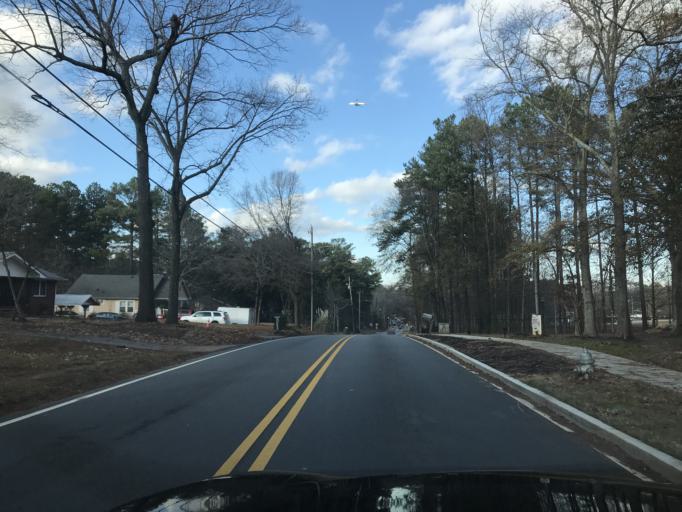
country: US
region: Georgia
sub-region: Fulton County
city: College Park
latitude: 33.6327
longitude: -84.4727
